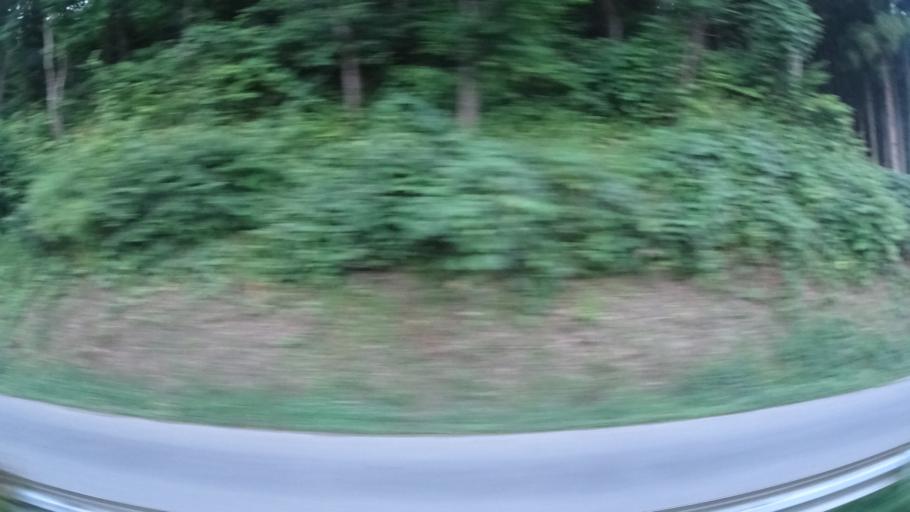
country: JP
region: Fukushima
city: Funehikimachi-funehiki
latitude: 37.2900
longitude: 140.6345
